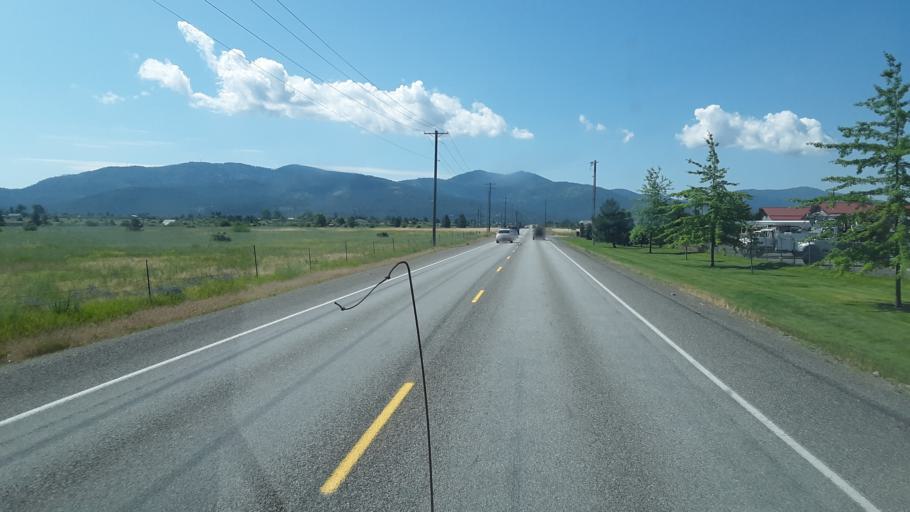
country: US
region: Idaho
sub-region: Kootenai County
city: Post Falls
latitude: 47.7359
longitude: -117.0019
